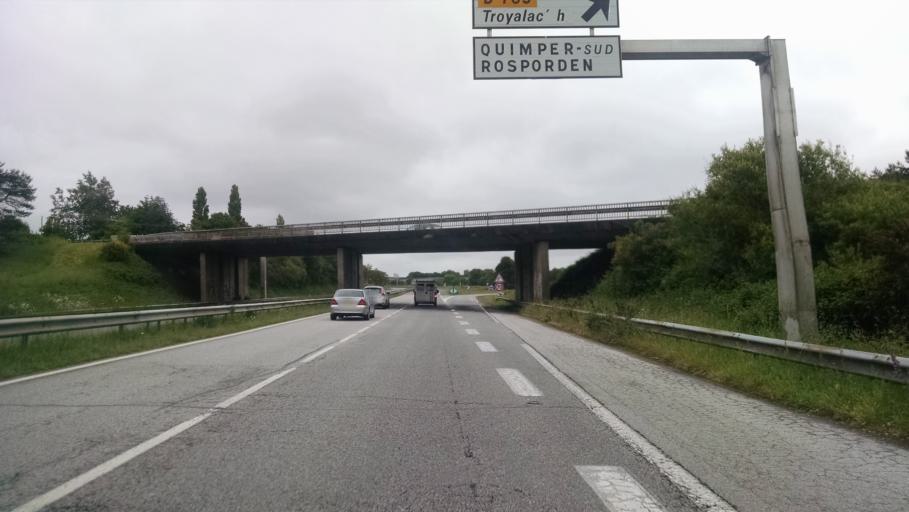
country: FR
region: Brittany
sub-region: Departement du Finistere
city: Ergue-Gaberic
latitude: 47.9785
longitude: -4.0116
